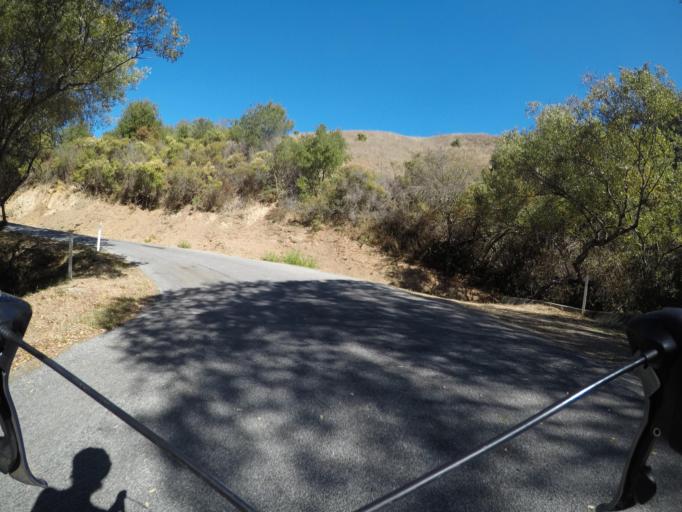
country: US
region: California
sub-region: San Mateo County
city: Portola Valley
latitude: 37.3600
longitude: -122.2531
